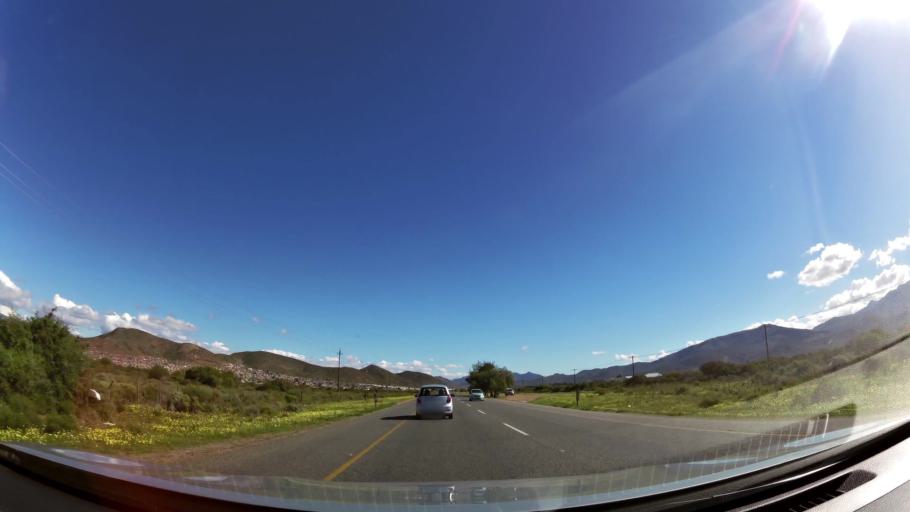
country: ZA
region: Western Cape
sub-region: Cape Winelands District Municipality
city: Ashton
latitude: -33.8147
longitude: 19.9078
